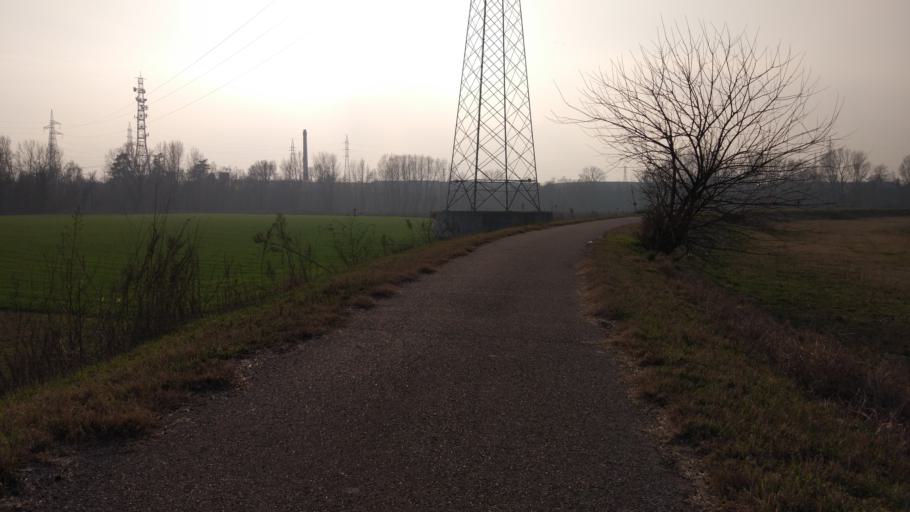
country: IT
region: Veneto
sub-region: Provincia di Verona
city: San Giovanni Lupatoto
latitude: 45.3958
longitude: 11.0381
